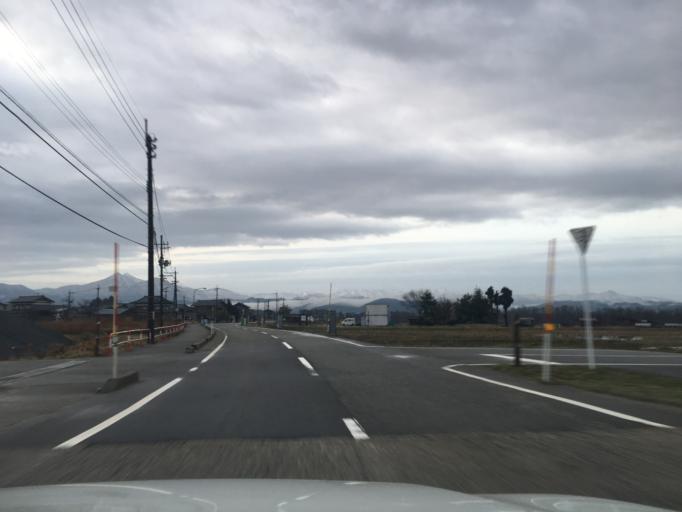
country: JP
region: Niigata
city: Murakami
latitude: 38.2764
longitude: 139.5228
